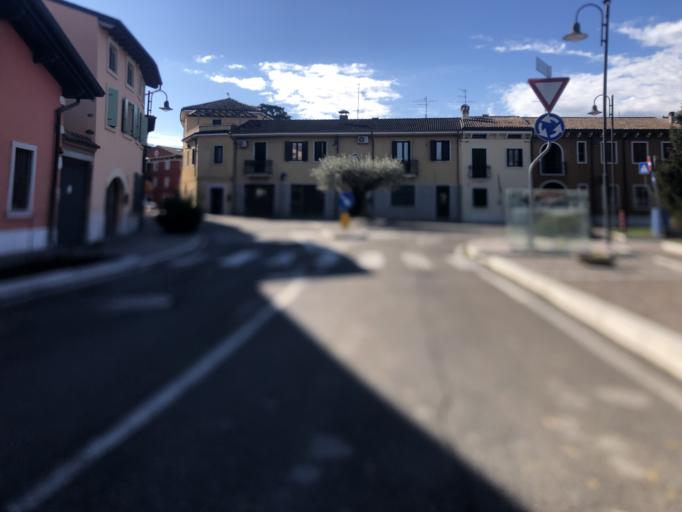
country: IT
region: Veneto
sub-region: Provincia di Verona
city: Bussolengo
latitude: 45.4817
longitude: 10.8463
